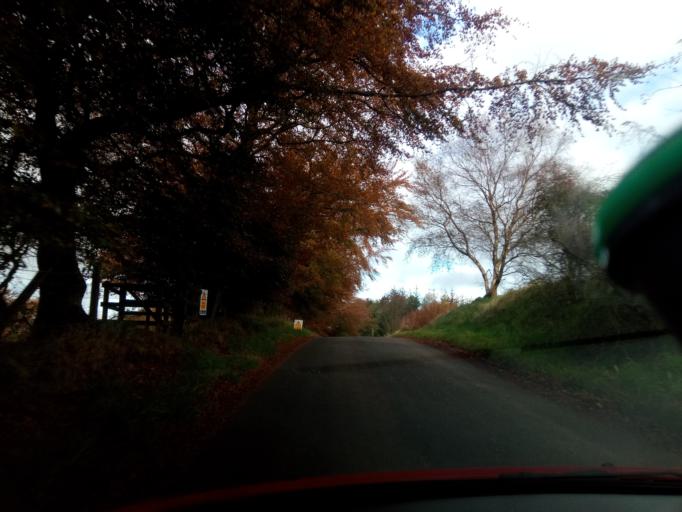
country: GB
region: Scotland
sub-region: South Lanarkshire
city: Carnwath
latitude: 55.7447
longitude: -3.6052
